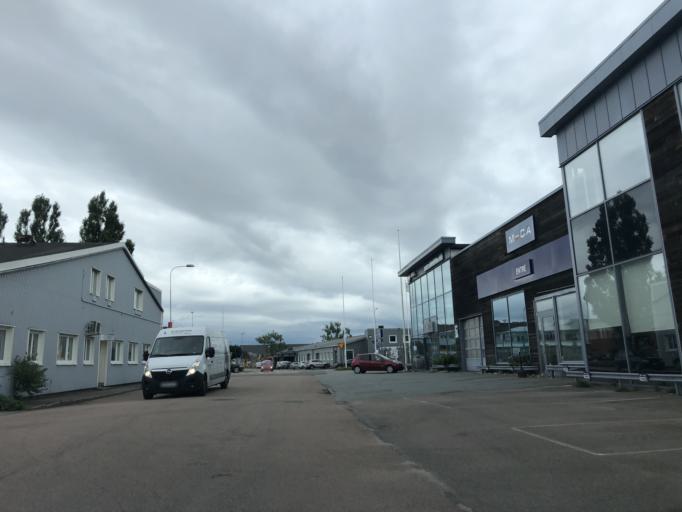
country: SE
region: Vaestra Goetaland
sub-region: Goteborg
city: Goeteborg
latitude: 57.7238
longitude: 11.9754
